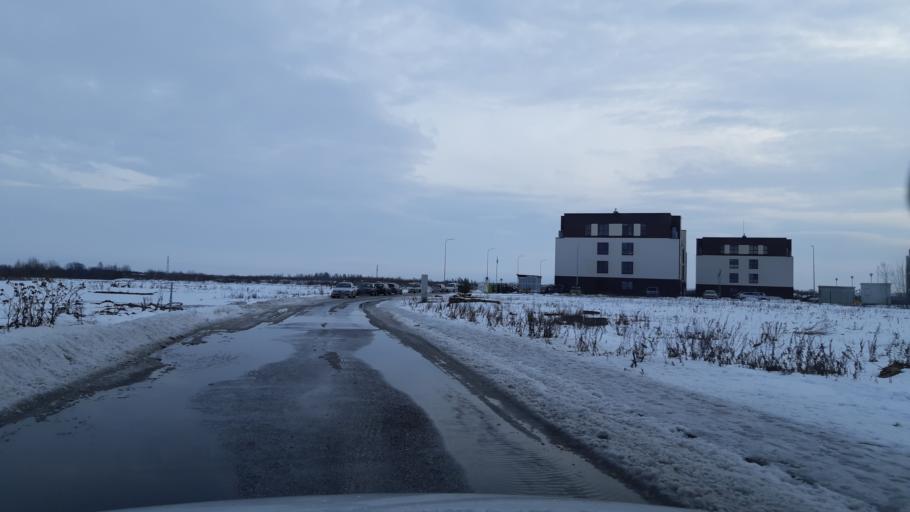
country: LT
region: Kauno apskritis
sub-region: Kauno rajonas
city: Garliava
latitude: 54.8384
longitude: 23.9055
